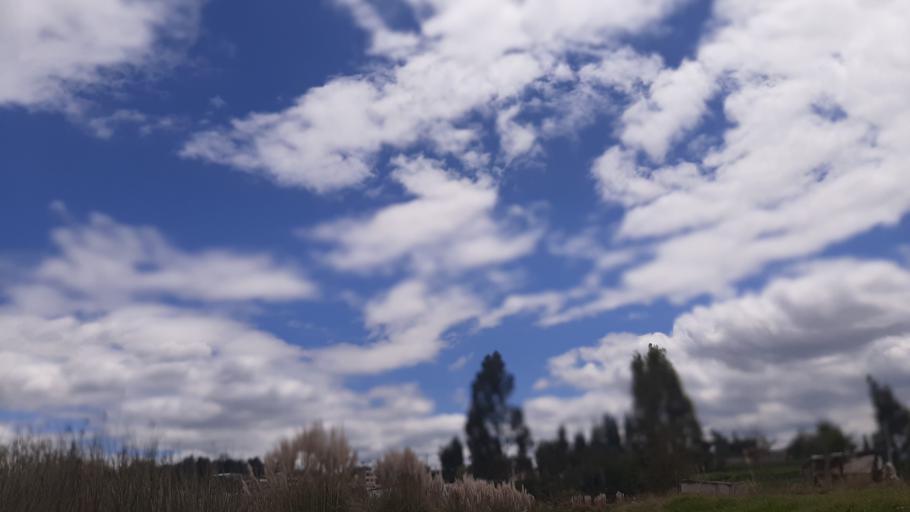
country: EC
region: Chimborazo
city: Riobamba
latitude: -1.6499
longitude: -78.6383
